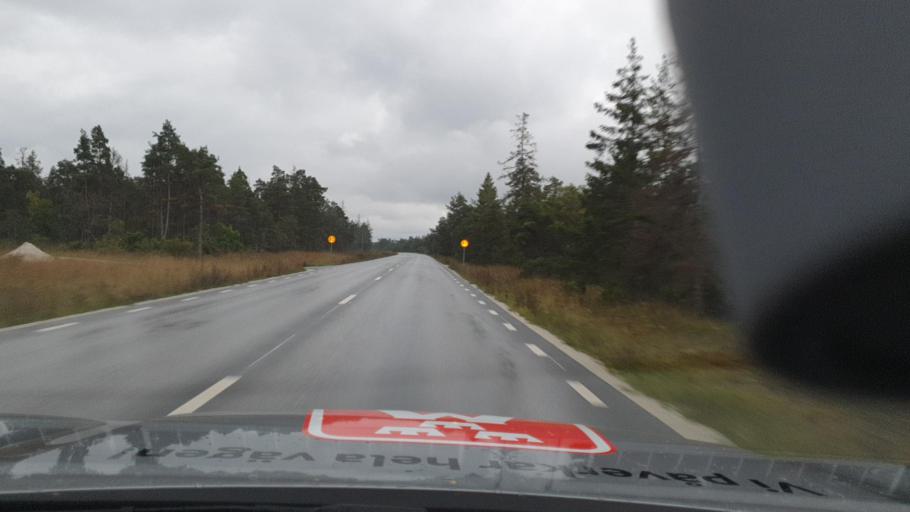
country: SE
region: Gotland
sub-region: Gotland
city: Slite
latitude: 57.7499
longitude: 18.7898
